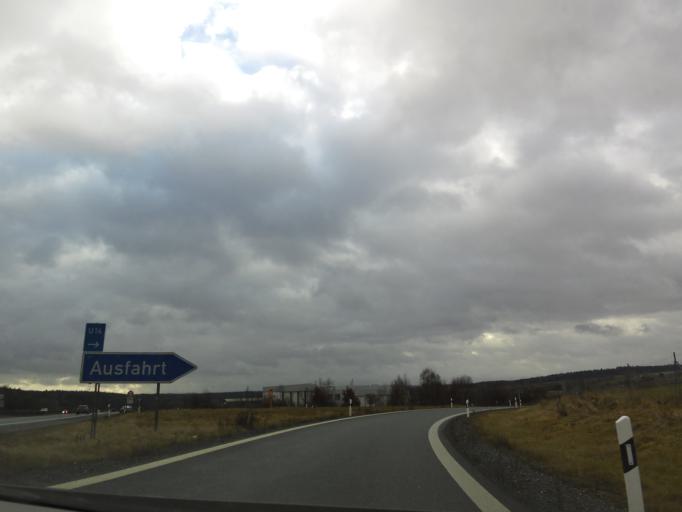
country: DE
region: Bavaria
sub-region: Upper Franconia
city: Selb
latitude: 50.1694
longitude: 12.1069
